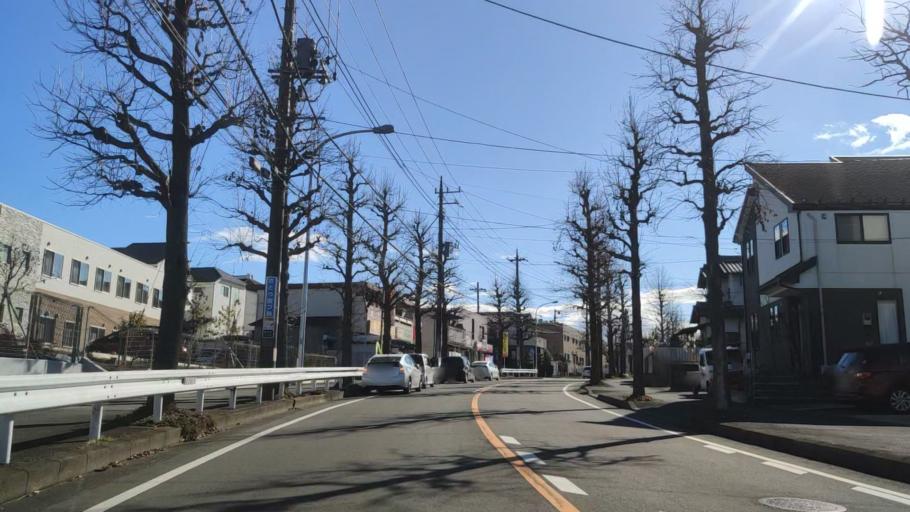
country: JP
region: Tokyo
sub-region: Machida-shi
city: Machida
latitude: 35.5185
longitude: 139.5082
